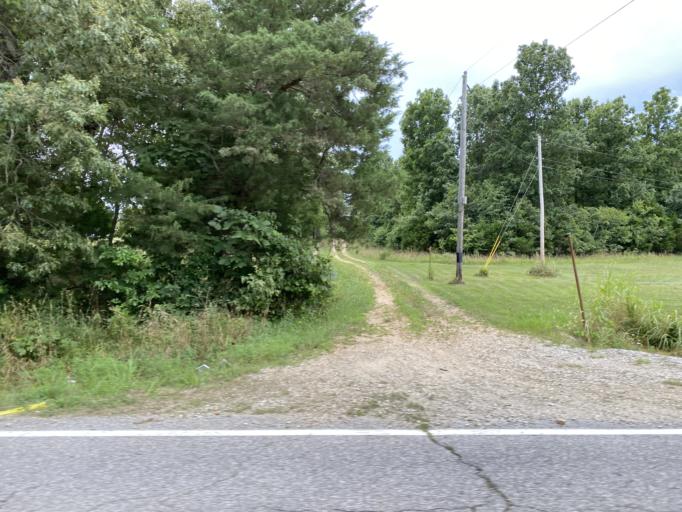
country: US
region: Arkansas
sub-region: Fulton County
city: Salem
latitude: 36.4174
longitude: -91.7224
